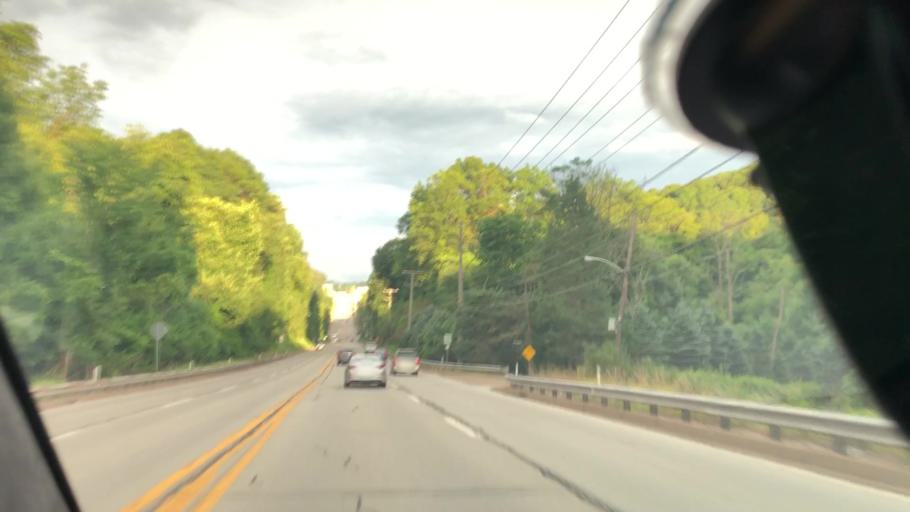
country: US
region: Pennsylvania
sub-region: Allegheny County
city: Churchill
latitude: 40.4368
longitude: -79.8275
